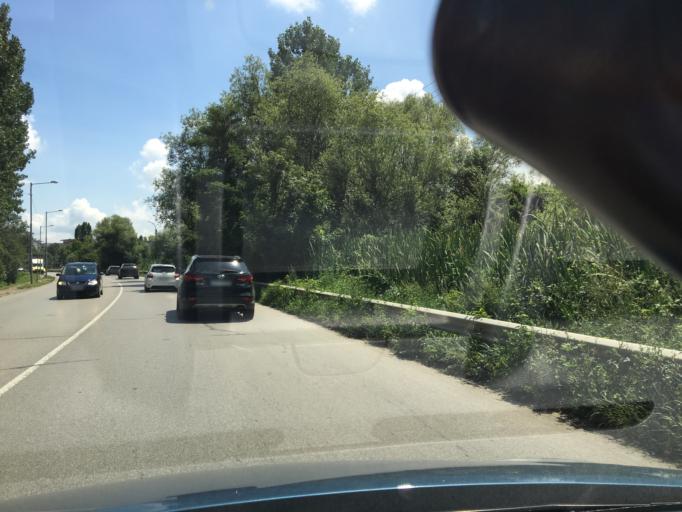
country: BG
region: Sofia-Capital
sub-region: Stolichna Obshtina
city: Sofia
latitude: 42.6584
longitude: 23.3069
